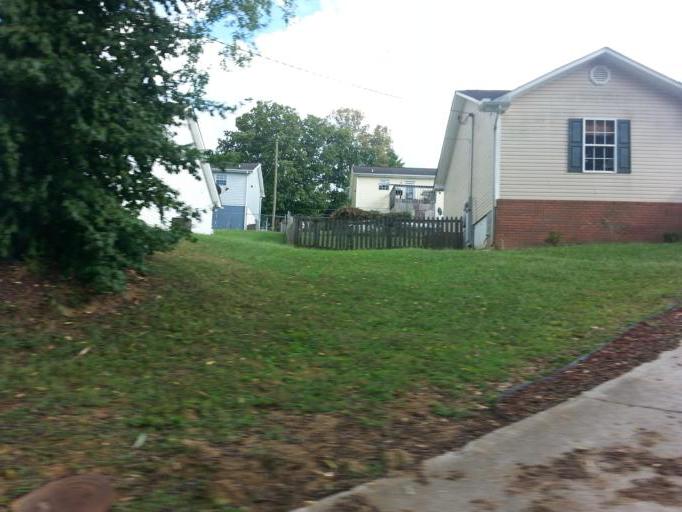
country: US
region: Tennessee
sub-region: Knox County
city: Knoxville
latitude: 36.0090
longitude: -83.9042
